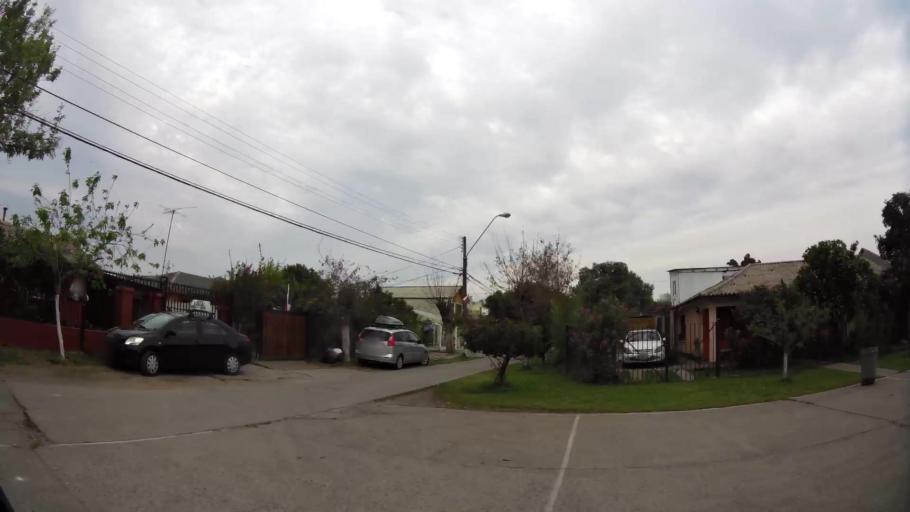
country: CL
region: Santiago Metropolitan
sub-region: Provincia de Santiago
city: Lo Prado
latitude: -33.5000
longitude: -70.7657
